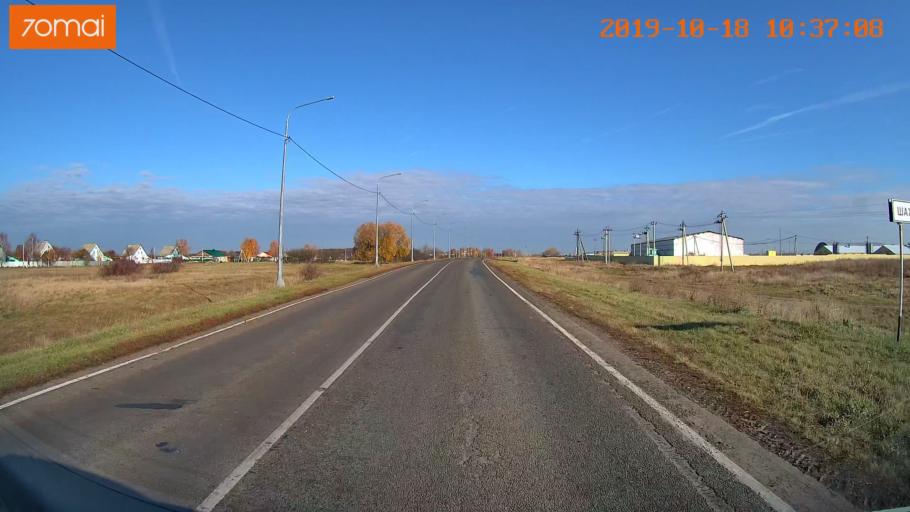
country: RU
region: Tula
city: Kurkino
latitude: 53.5586
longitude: 38.6298
